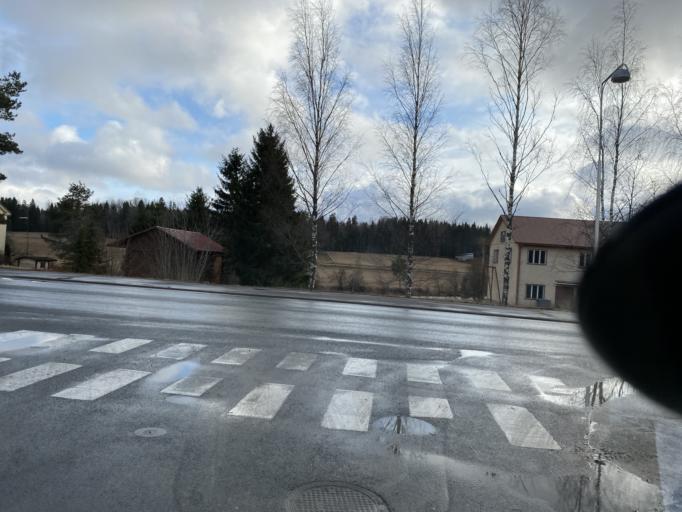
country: FI
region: Pirkanmaa
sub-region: Lounais-Pirkanmaa
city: Punkalaidun
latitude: 61.1173
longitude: 23.0870
